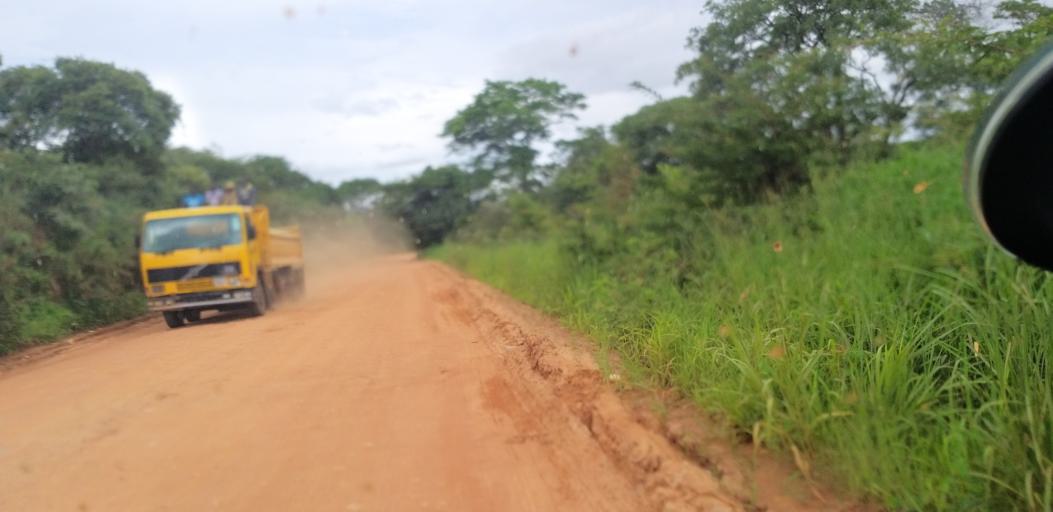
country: ZM
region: Lusaka
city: Lusaka
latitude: -15.2001
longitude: 28.4397
